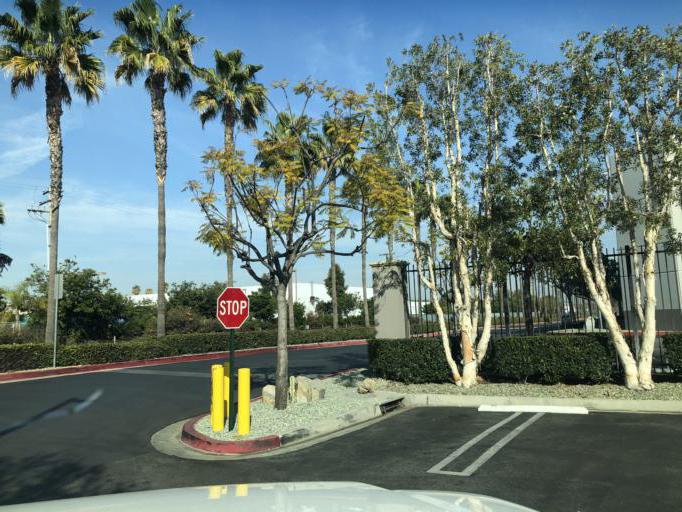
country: US
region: California
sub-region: Orange County
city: Irvine
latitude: 33.6902
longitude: -117.8470
